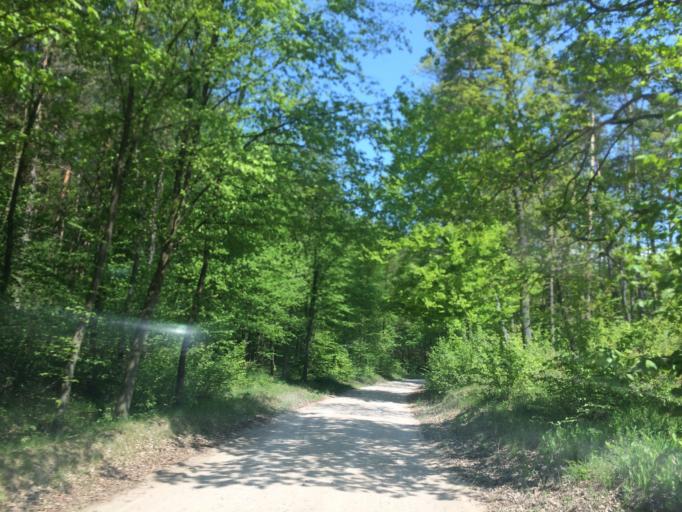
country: PL
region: Warmian-Masurian Voivodeship
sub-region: Powiat nowomiejski
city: Nowe Miasto Lubawskie
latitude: 53.4507
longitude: 19.6315
